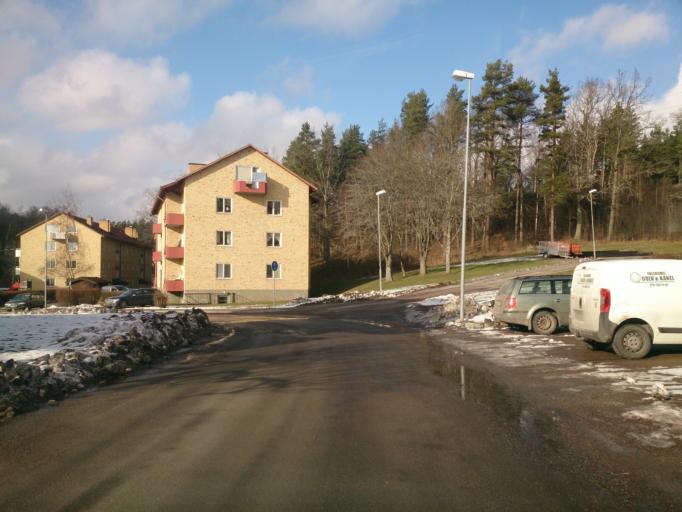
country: SE
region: OEstergoetland
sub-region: Atvidabergs Kommun
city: Atvidaberg
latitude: 58.2049
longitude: 16.0101
